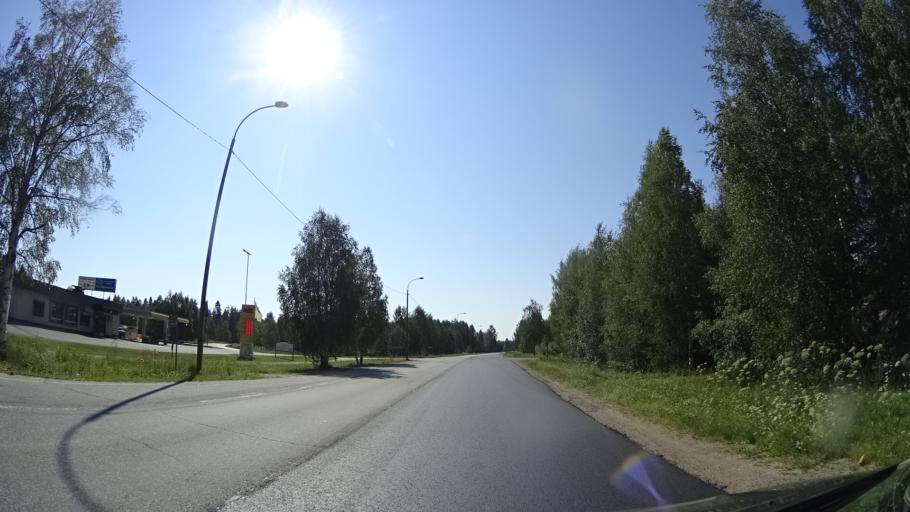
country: FI
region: North Karelia
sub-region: Joensuu
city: Juuka
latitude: 63.2405
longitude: 29.2796
